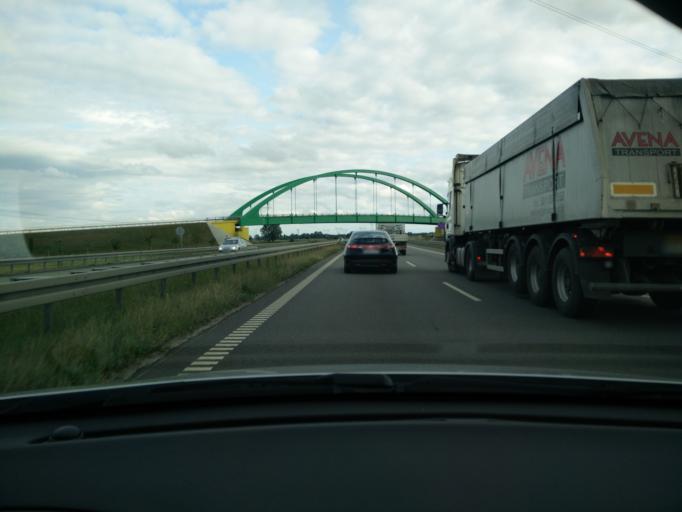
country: PL
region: Pomeranian Voivodeship
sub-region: Gdansk
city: Gdansk
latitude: 54.3338
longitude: 18.7032
